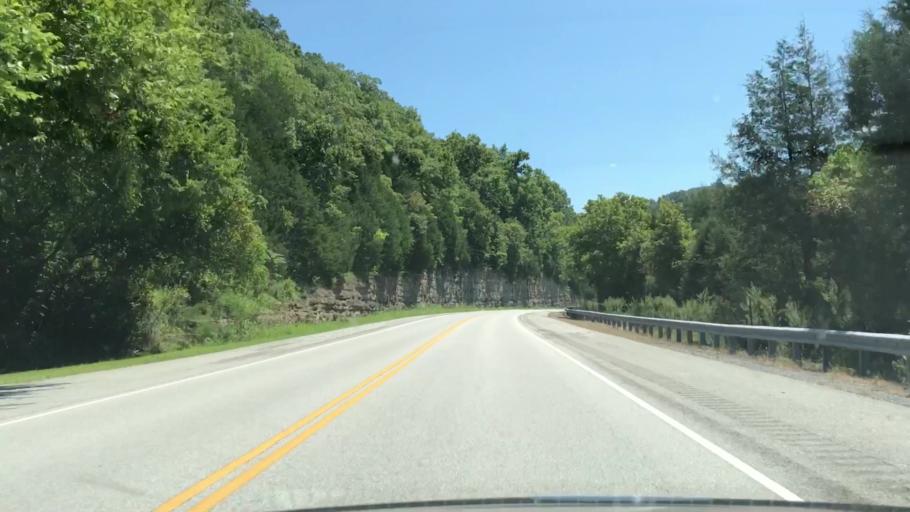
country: US
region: Tennessee
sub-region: Clay County
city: Celina
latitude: 36.4674
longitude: -85.5807
